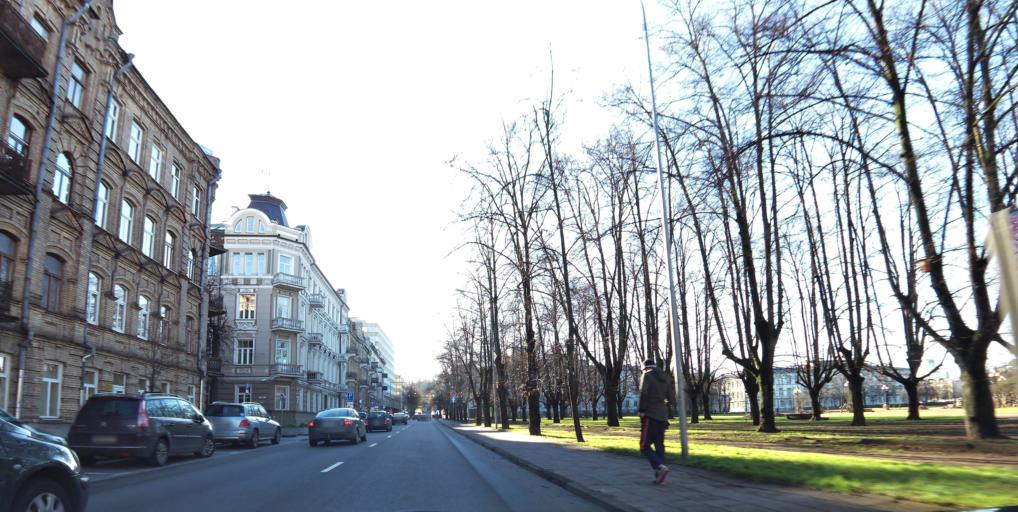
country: LT
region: Vilnius County
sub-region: Vilnius
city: Vilnius
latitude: 54.6900
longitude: 25.2727
